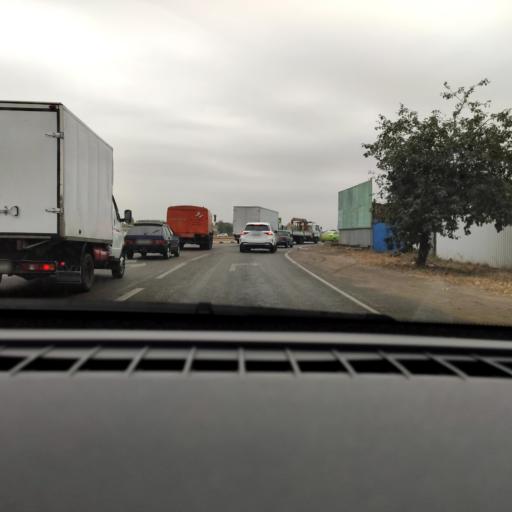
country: RU
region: Voronezj
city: Voronezh
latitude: 51.6657
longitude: 39.2708
